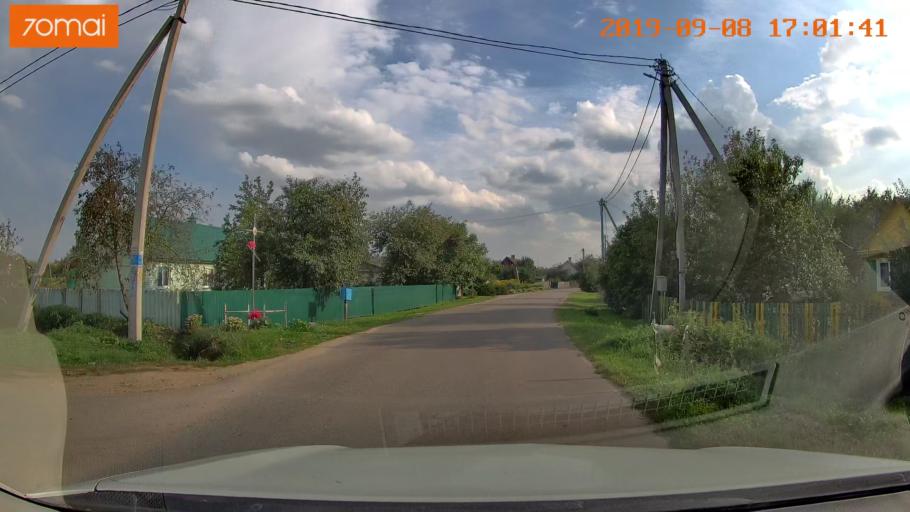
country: BY
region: Grodnenskaya
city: Hrodna
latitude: 53.7085
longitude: 23.9365
